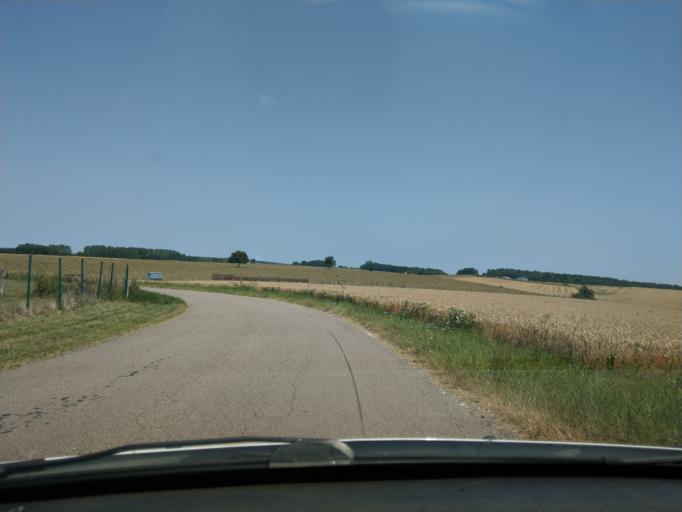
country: FR
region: Lorraine
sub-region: Departement de Meurthe-et-Moselle
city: Baccarat
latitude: 48.5845
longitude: 6.7438
